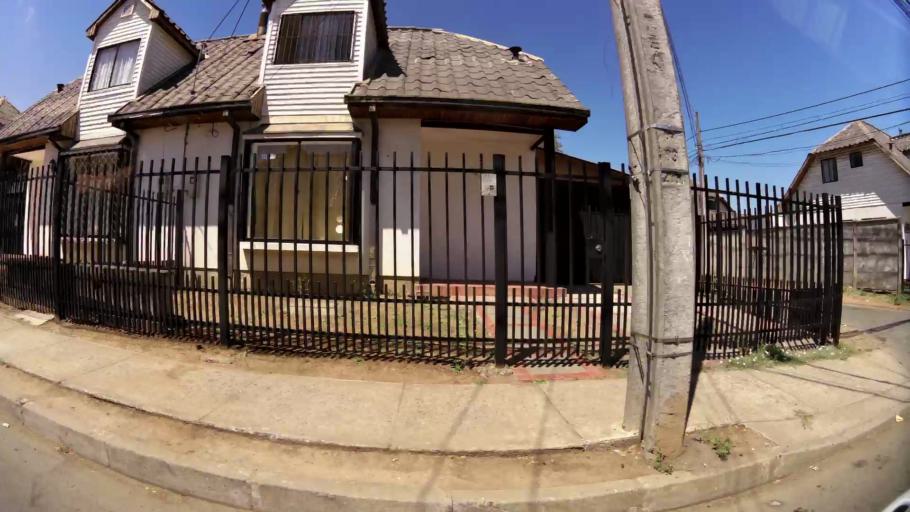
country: CL
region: Maule
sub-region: Provincia de Talca
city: Talca
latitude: -35.4286
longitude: -71.6242
